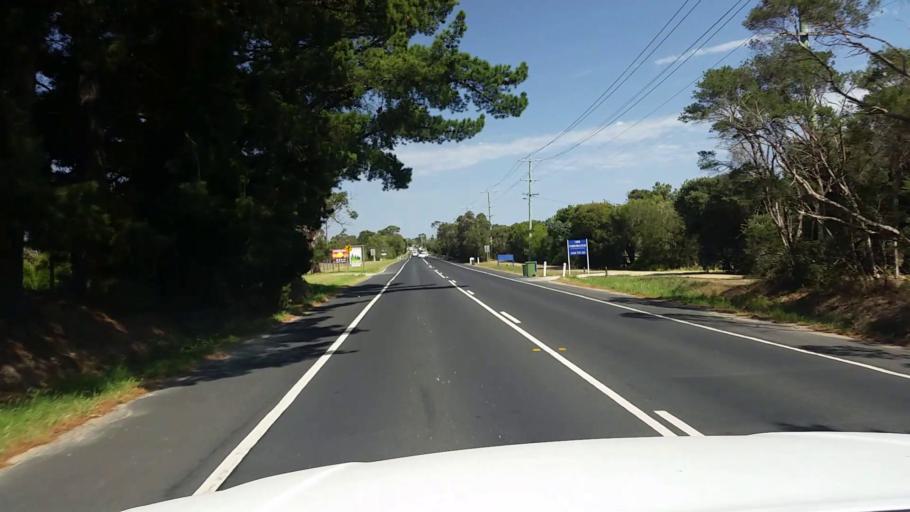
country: AU
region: Victoria
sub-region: Mornington Peninsula
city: Tyabb
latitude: -38.2491
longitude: 145.1912
